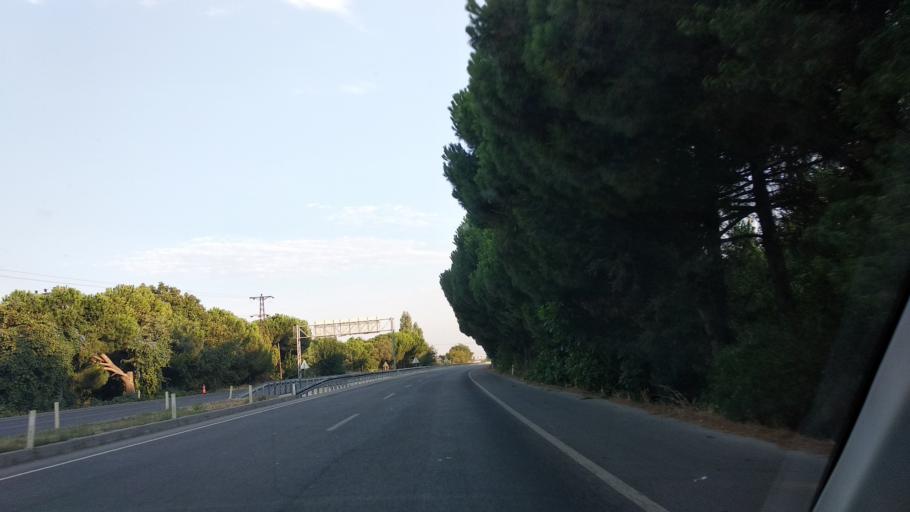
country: TR
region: Izmir
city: Dikili
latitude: 39.0815
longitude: 26.9216
